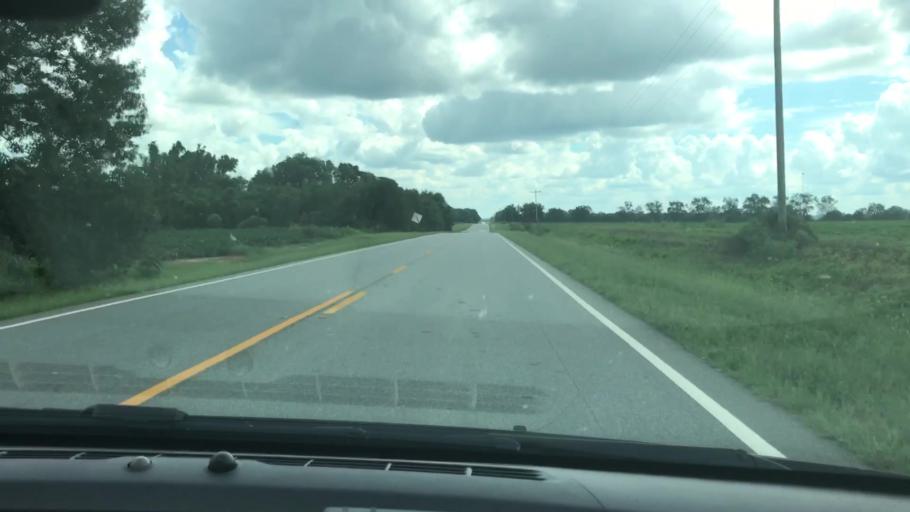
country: US
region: Georgia
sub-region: Quitman County
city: Georgetown
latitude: 31.8114
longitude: -85.0935
